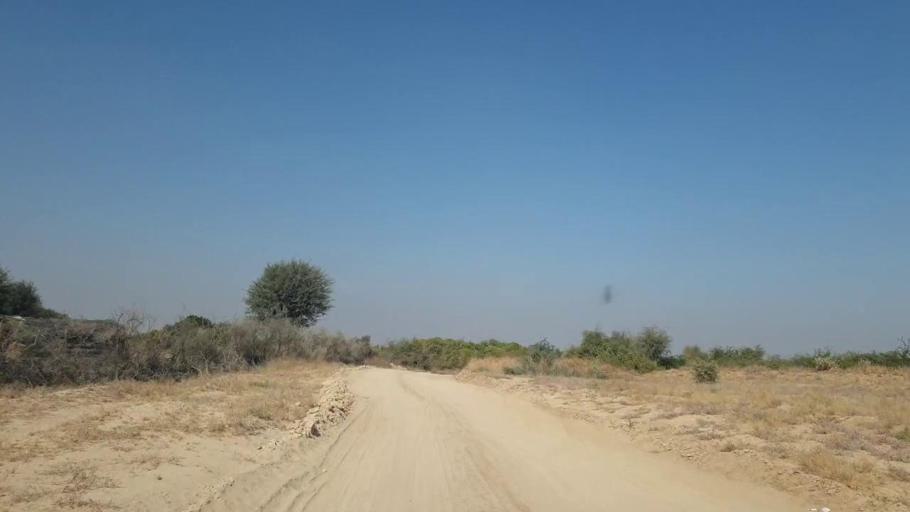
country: PK
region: Sindh
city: Jamshoro
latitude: 25.3016
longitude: 67.8159
